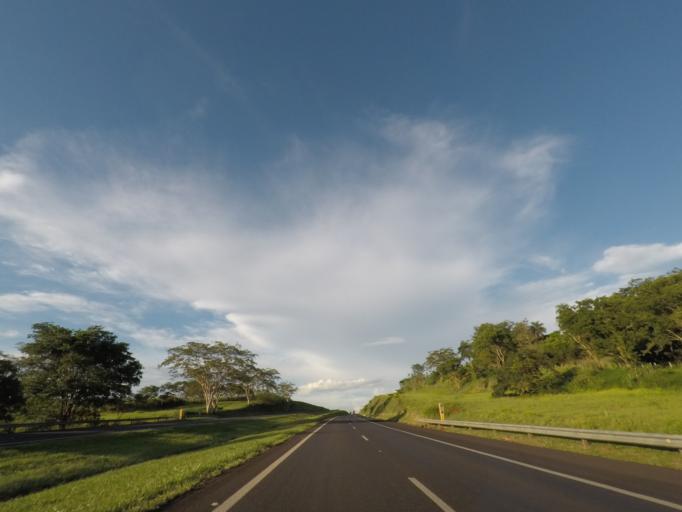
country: BR
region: Sao Paulo
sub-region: Ituverava
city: Ituverava
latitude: -20.2526
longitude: -47.7995
